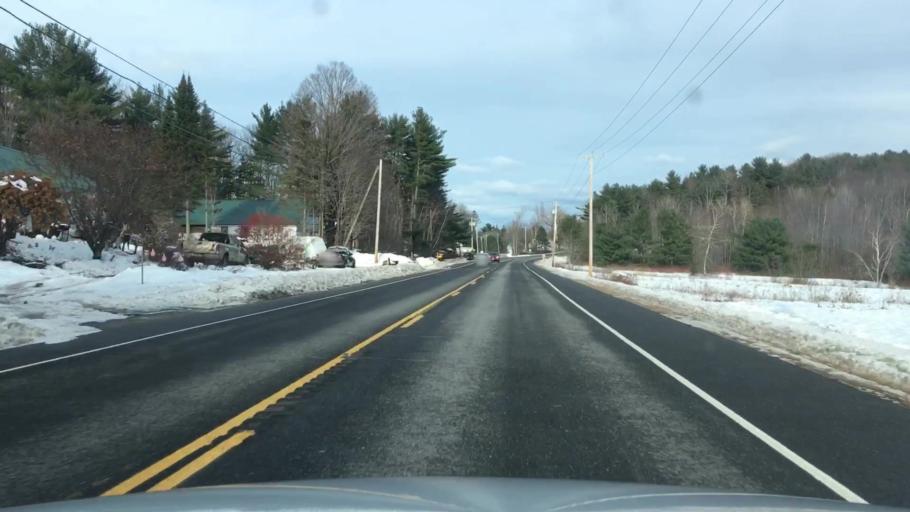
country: US
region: Maine
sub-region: Androscoggin County
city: Greene
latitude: 44.2128
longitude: -70.0978
